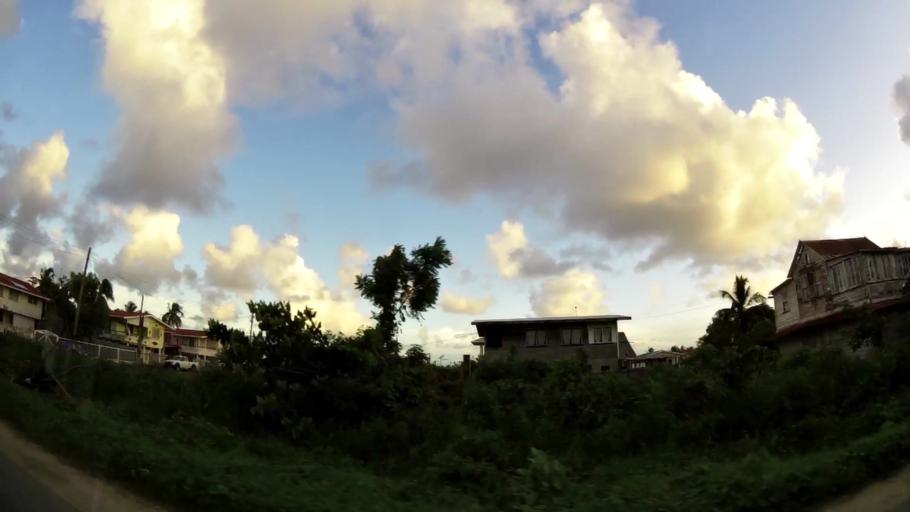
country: GY
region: Demerara-Mahaica
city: Georgetown
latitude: 6.8156
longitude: -58.1109
